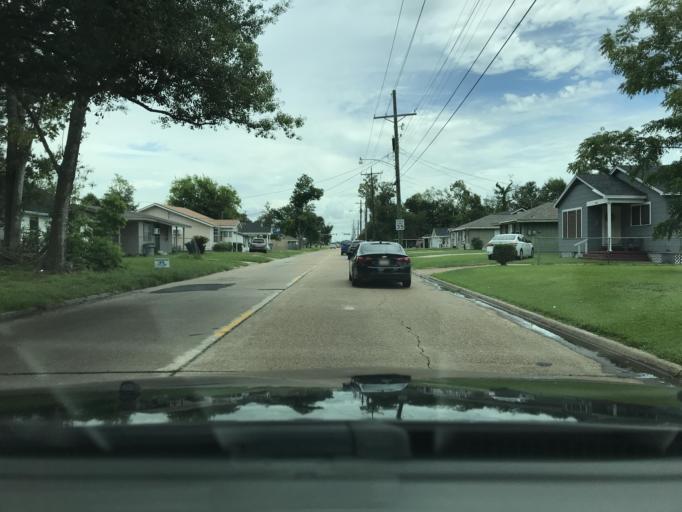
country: US
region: Louisiana
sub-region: Calcasieu Parish
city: Lake Charles
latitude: 30.2034
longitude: -93.2071
